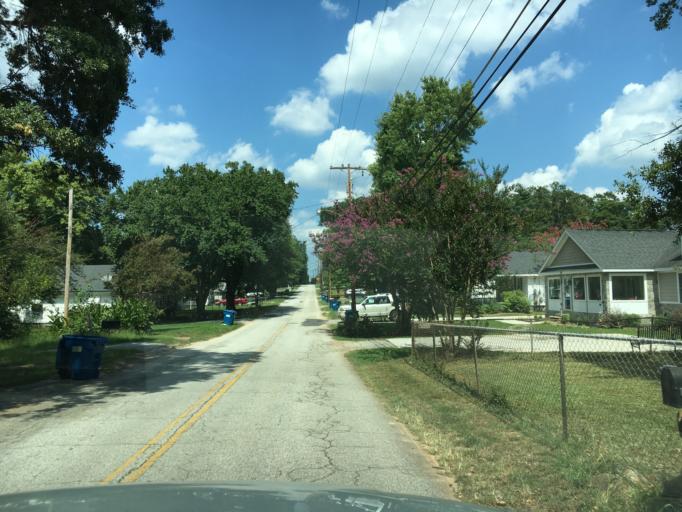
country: US
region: South Carolina
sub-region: Spartanburg County
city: Duncan
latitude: 34.9323
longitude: -82.1349
